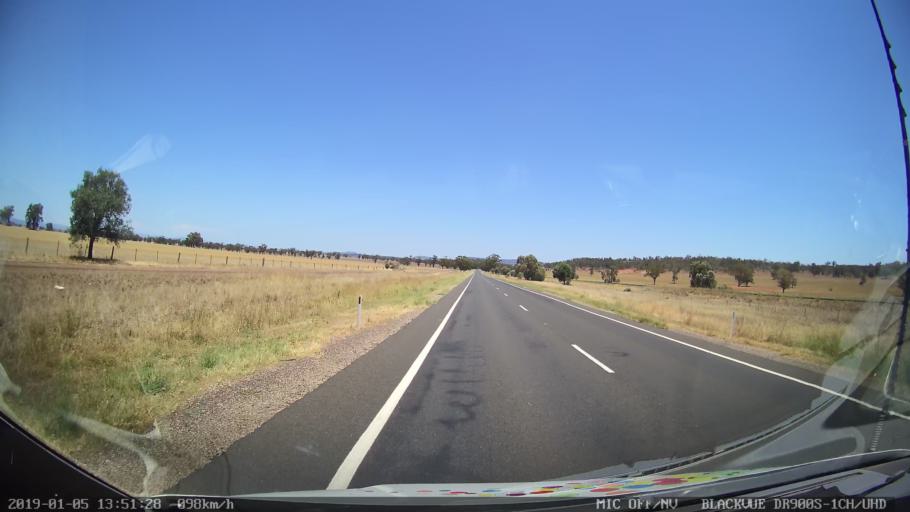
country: AU
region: New South Wales
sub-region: Gunnedah
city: Gunnedah
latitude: -31.0450
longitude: 150.2769
